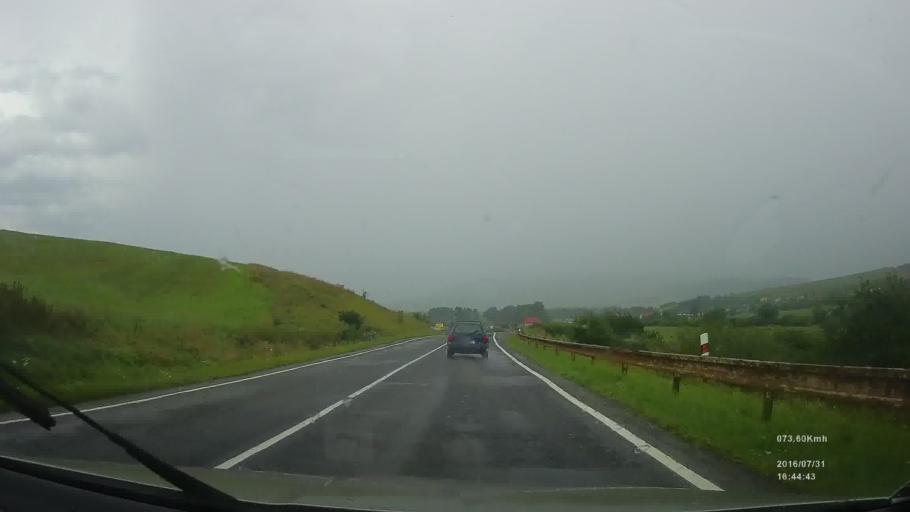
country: SK
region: Presovsky
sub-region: Okres Presov
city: Presov
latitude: 49.0734
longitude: 21.3298
